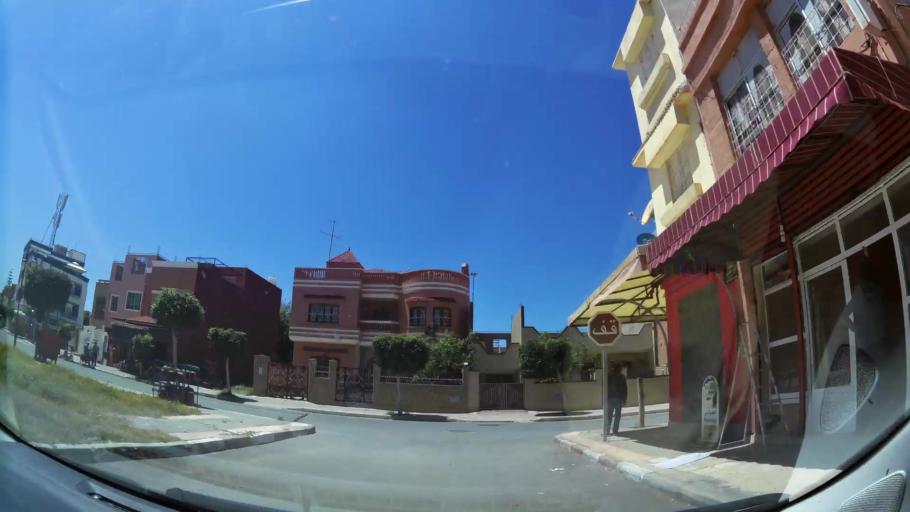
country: MA
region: Oriental
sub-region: Berkane-Taourirt
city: Madagh
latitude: 35.0819
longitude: -2.2218
